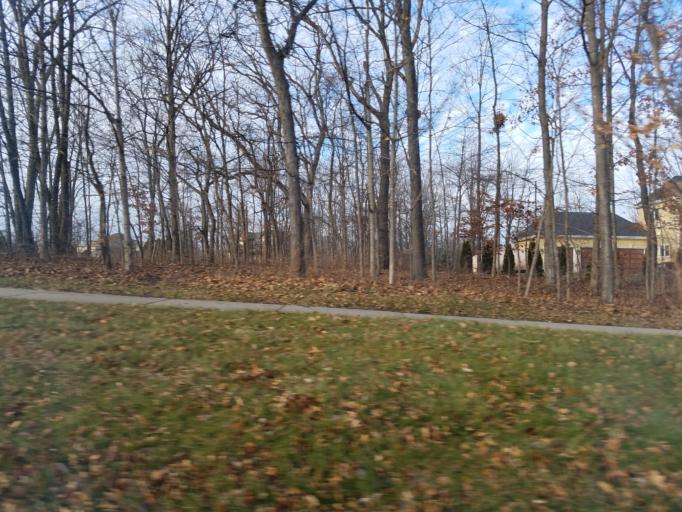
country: US
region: Illinois
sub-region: Will County
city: Mokena
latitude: 41.5274
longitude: -87.8693
